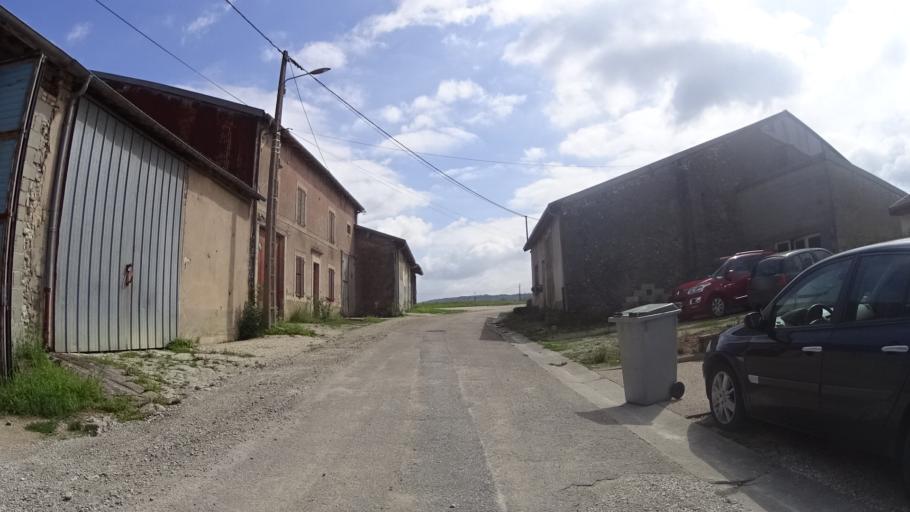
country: FR
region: Lorraine
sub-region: Departement de la Meuse
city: Ligny-en-Barrois
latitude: 48.7167
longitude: 5.3677
